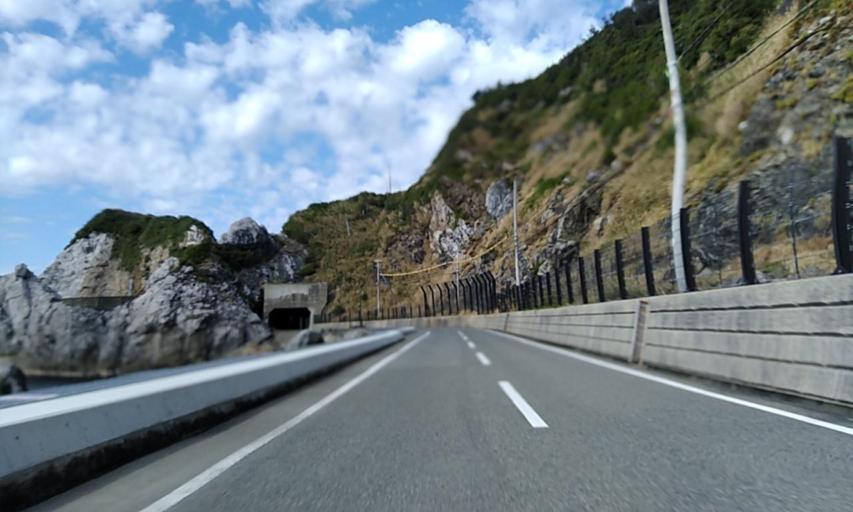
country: JP
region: Wakayama
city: Gobo
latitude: 33.9763
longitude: 135.0747
